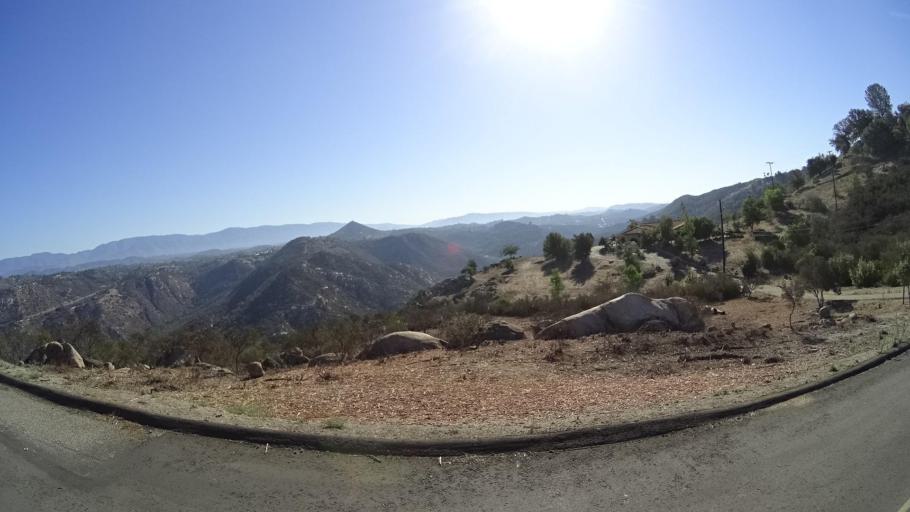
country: US
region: California
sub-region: San Diego County
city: Hidden Meadows
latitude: 33.2391
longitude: -117.1166
